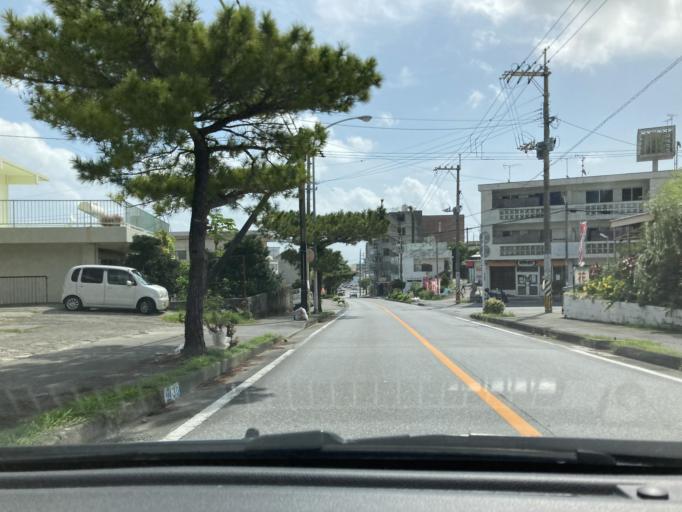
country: JP
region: Okinawa
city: Okinawa
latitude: 26.3208
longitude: 127.8194
